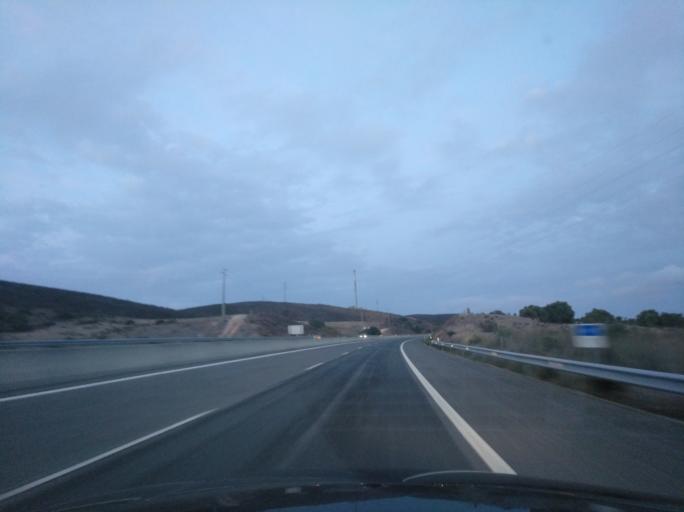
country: PT
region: Faro
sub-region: Lagos
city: Lagos
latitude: 37.1631
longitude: -8.6821
